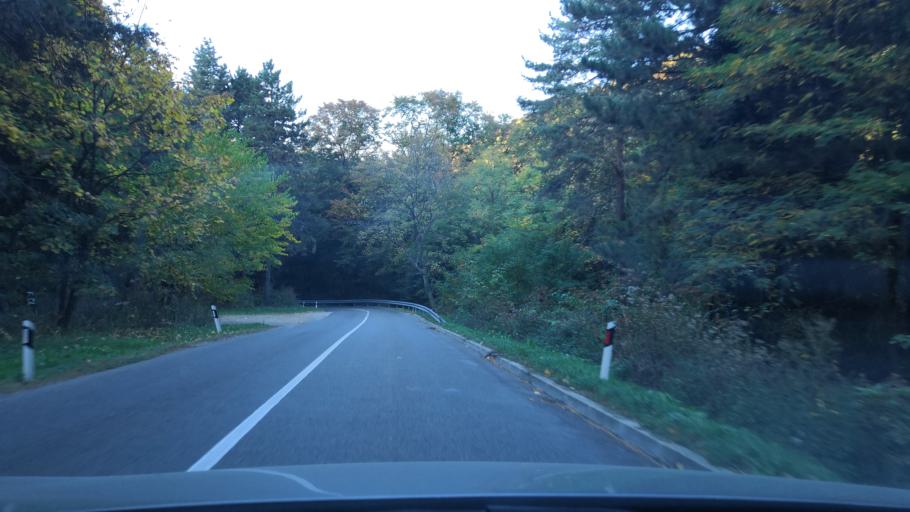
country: RS
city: Vrdnik
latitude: 45.1633
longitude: 19.7764
